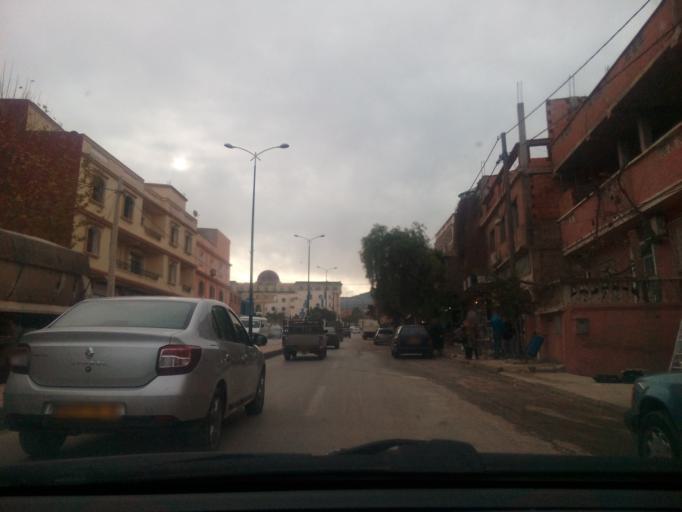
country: DZ
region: Tlemcen
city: Mansoura
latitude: 34.8810
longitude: -1.3494
